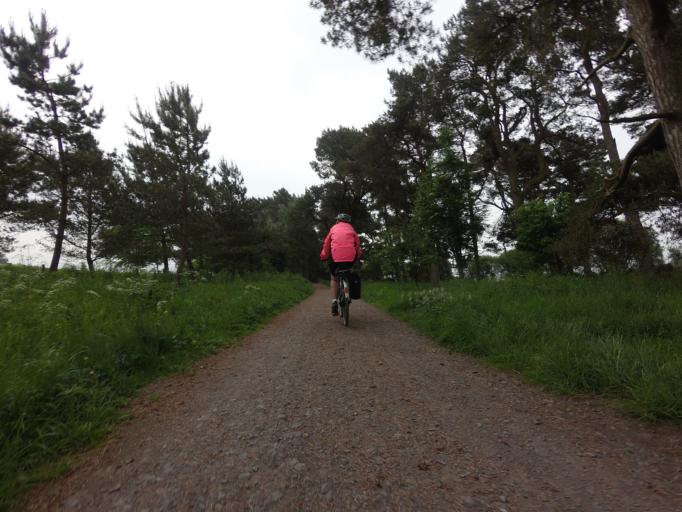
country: GB
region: Scotland
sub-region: Perth and Kinross
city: Milnathort
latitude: 56.2203
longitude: -3.3932
